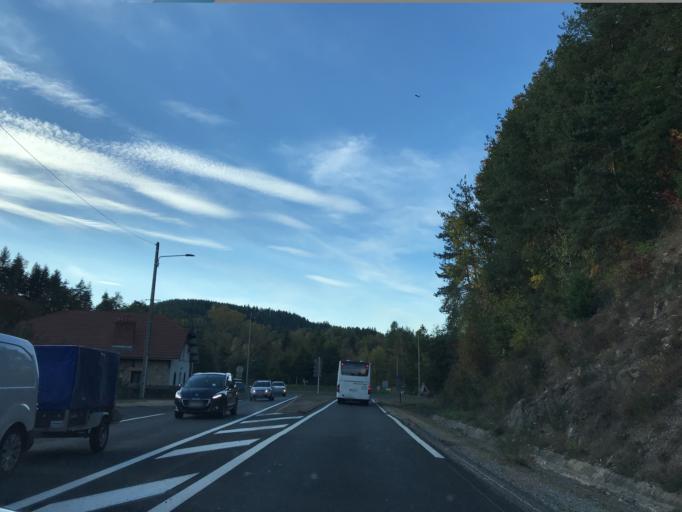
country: FR
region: Auvergne
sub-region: Departement du Puy-de-Dome
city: Celles-sur-Durolle
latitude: 45.8695
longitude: 3.6297
